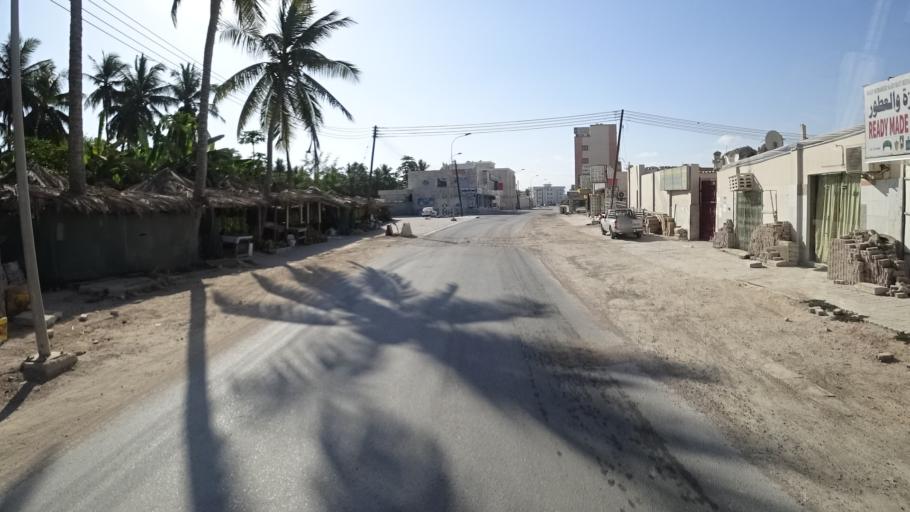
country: OM
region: Zufar
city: Salalah
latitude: 17.0092
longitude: 54.0989
